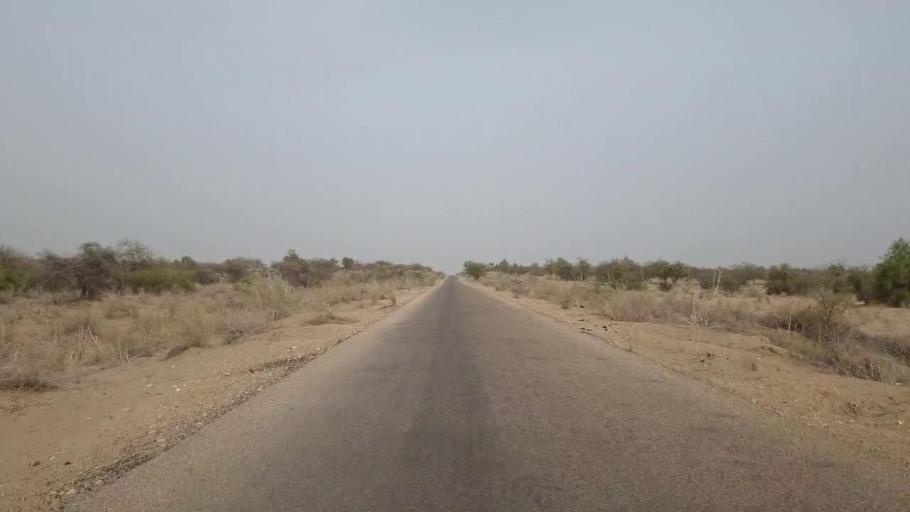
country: PK
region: Sindh
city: Islamkot
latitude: 24.5610
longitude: 70.3399
